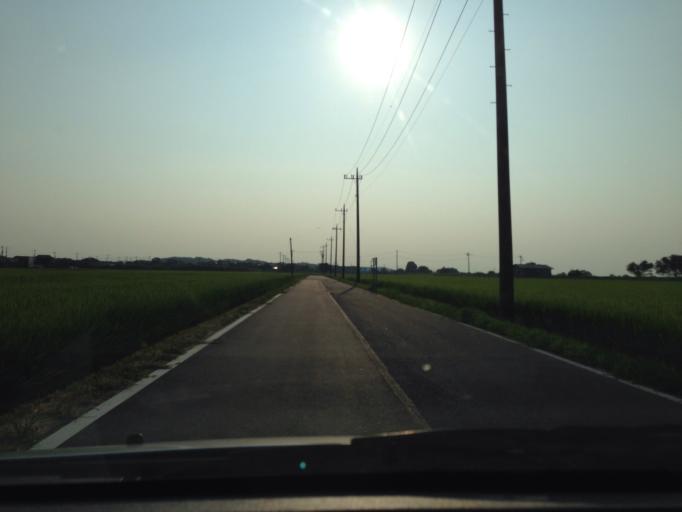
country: JP
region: Ibaraki
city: Inashiki
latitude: 36.0257
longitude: 140.3029
